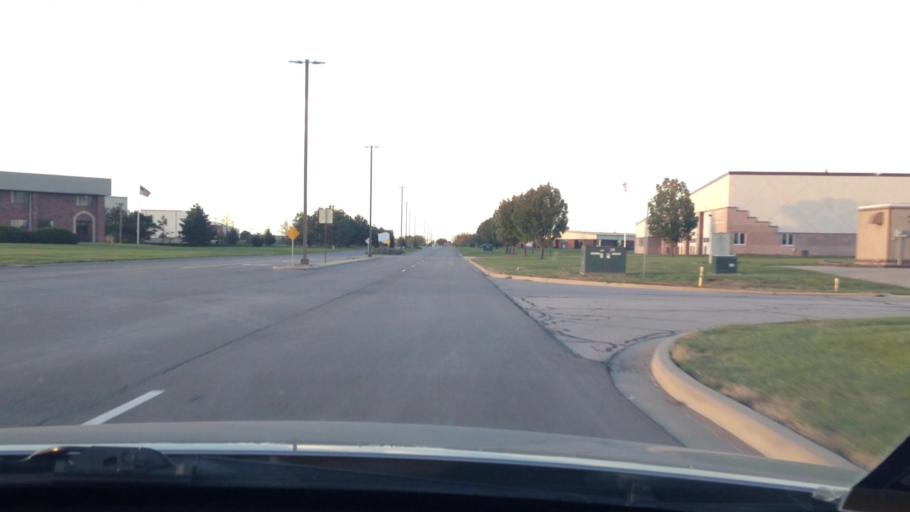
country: US
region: Kansas
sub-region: Johnson County
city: Gardner
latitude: 38.8287
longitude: -94.9053
